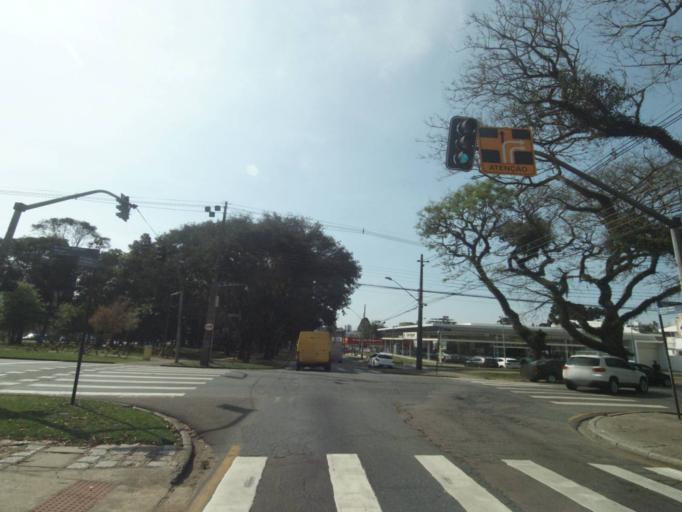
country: BR
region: Parana
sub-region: Curitiba
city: Curitiba
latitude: -25.4570
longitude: -49.3029
